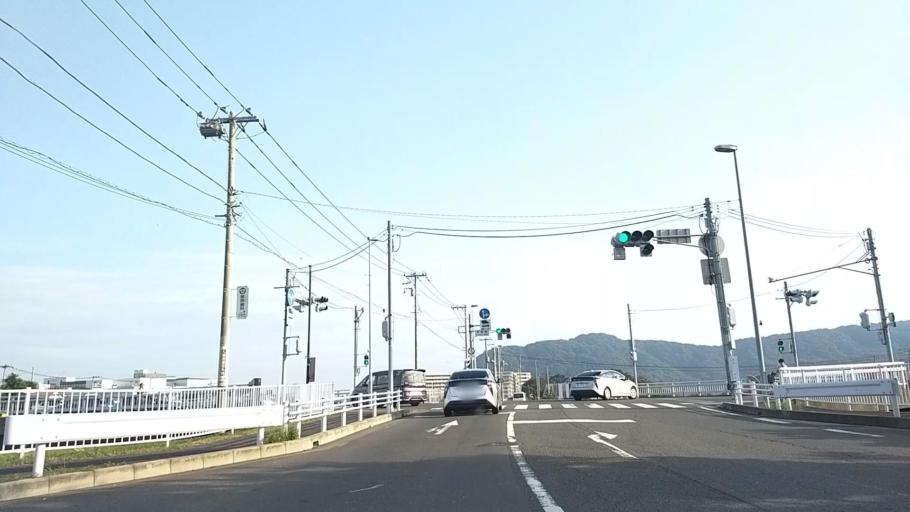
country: JP
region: Kanagawa
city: Hiratsuka
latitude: 35.3405
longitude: 139.3222
